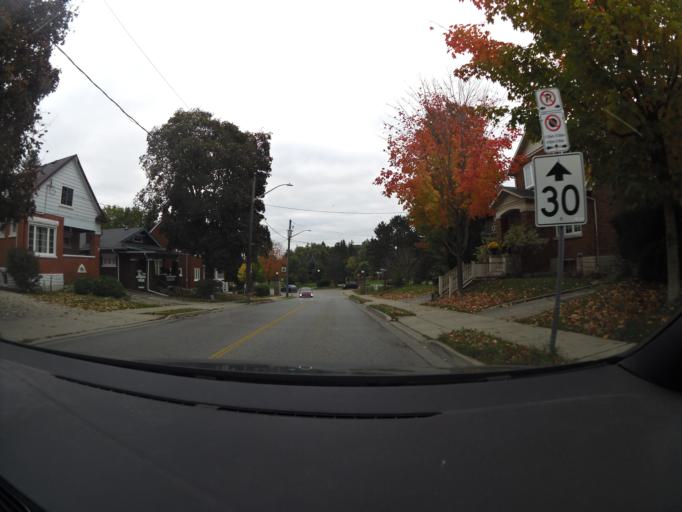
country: CA
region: Ontario
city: Kitchener
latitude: 43.4474
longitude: -80.5010
